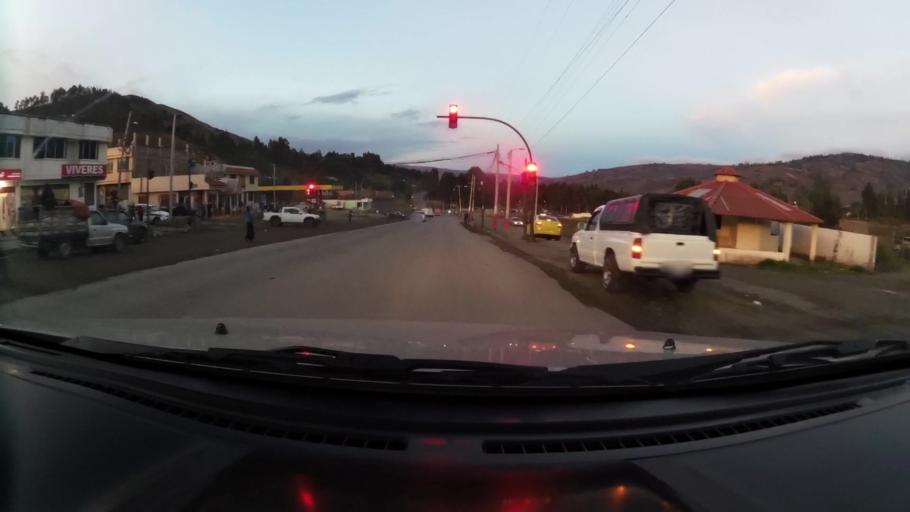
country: EC
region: Chimborazo
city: Riobamba
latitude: -1.9325
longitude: -78.7059
